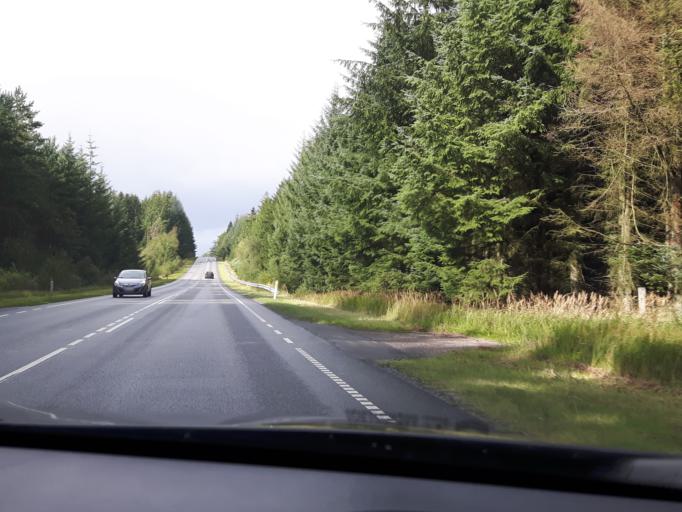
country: DK
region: North Denmark
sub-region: Jammerbugt Kommune
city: Fjerritslev
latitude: 57.0886
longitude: 9.3929
